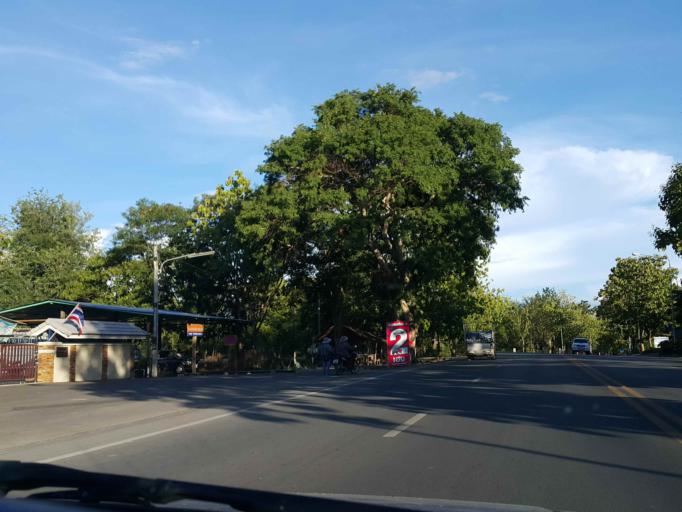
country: TH
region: Chiang Mai
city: Chom Thong
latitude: 18.4492
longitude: 98.6751
